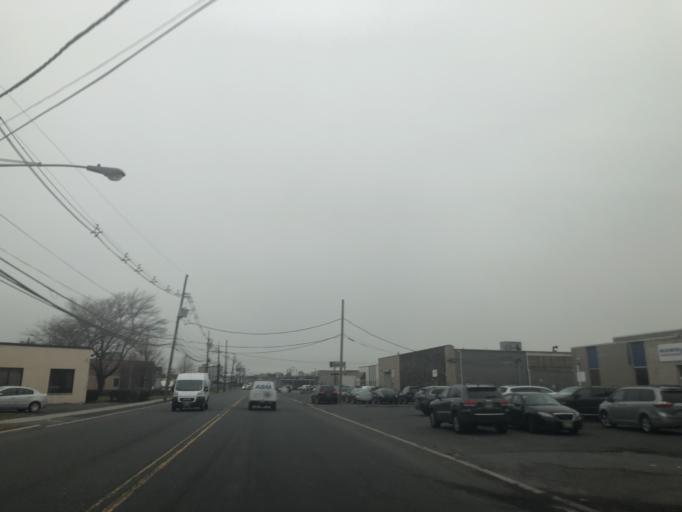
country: US
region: New Jersey
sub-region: Union County
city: Elizabeth
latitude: 40.6695
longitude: -74.1888
